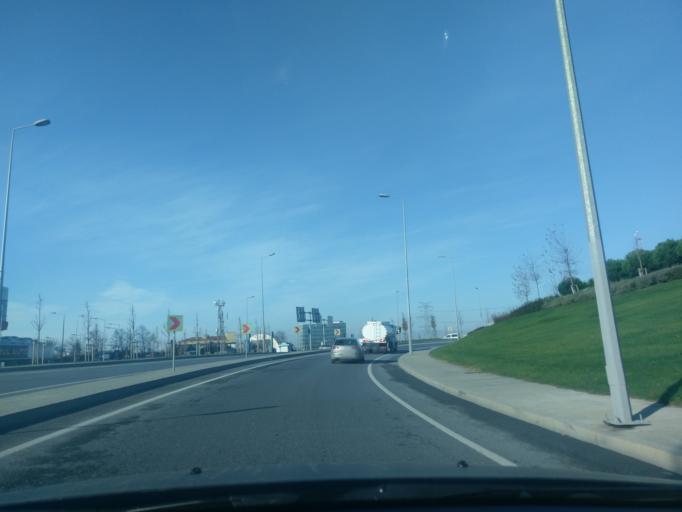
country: TR
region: Istanbul
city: Mahmutbey
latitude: 41.0677
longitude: 28.8351
